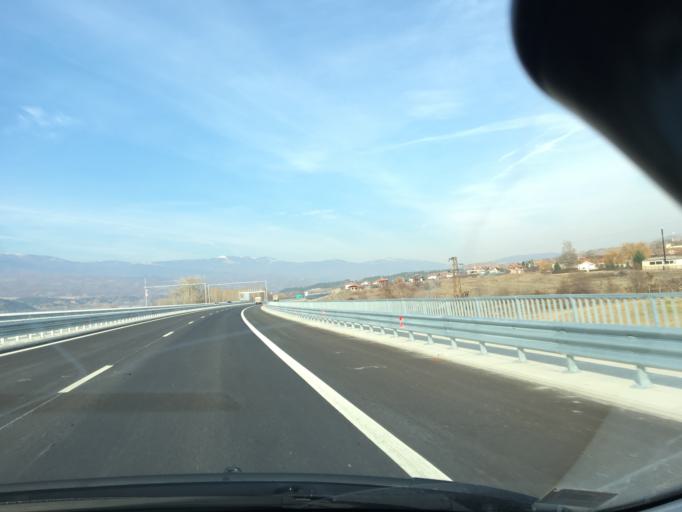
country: BG
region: Blagoevgrad
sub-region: Obshtina Strumyani
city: Strumyani
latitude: 41.6315
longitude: 23.1994
